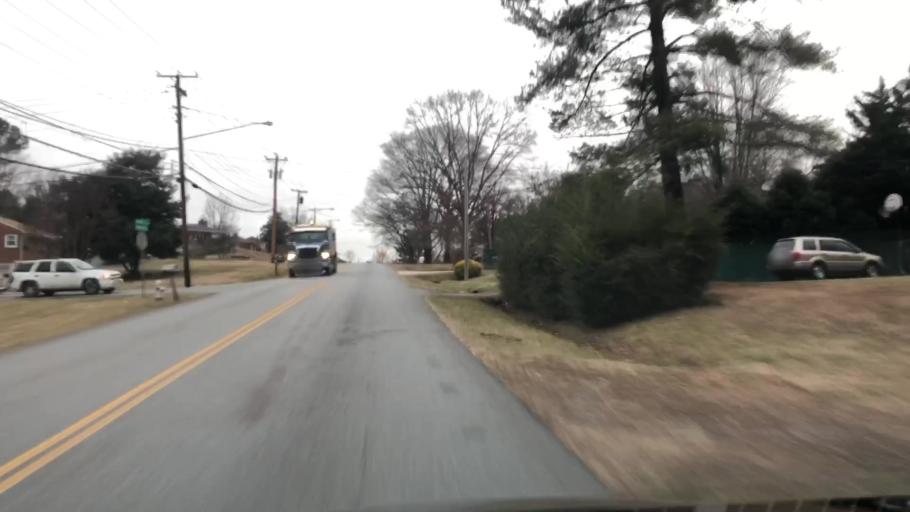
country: US
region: Virginia
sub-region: City of Lynchburg
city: West Lynchburg
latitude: 37.3464
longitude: -79.1923
